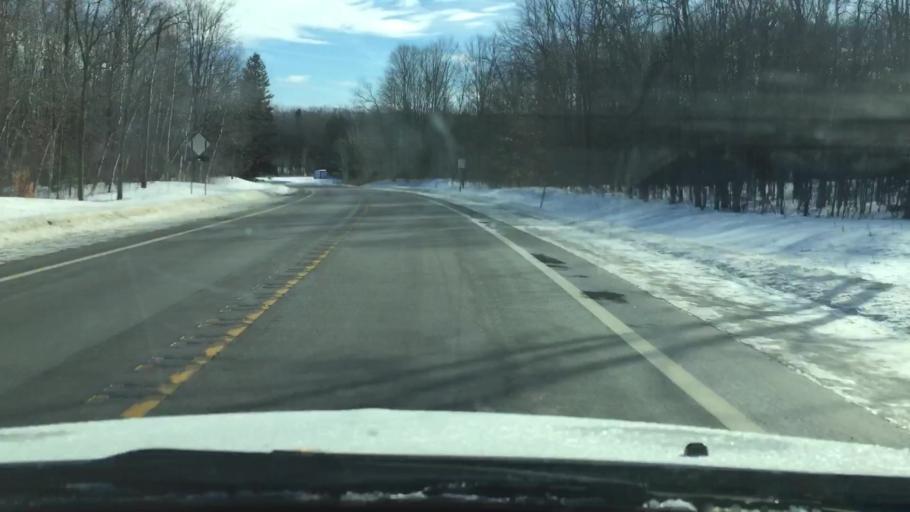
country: US
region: Michigan
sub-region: Antrim County
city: Mancelona
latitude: 44.9913
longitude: -85.0615
